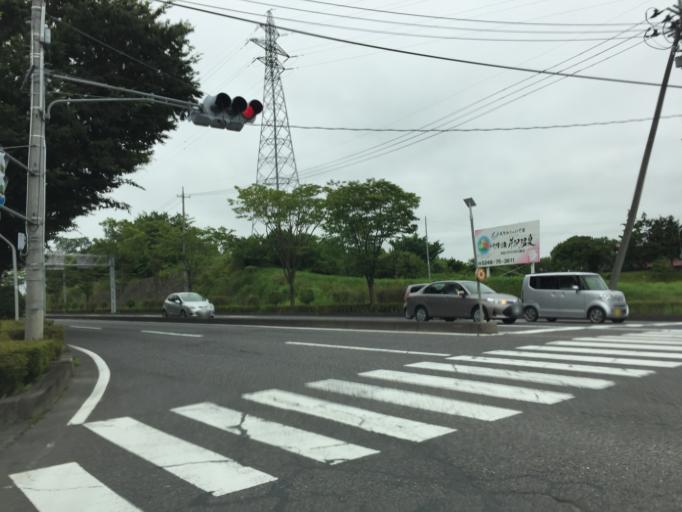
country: JP
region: Fukushima
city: Sukagawa
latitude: 37.2767
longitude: 140.3584
